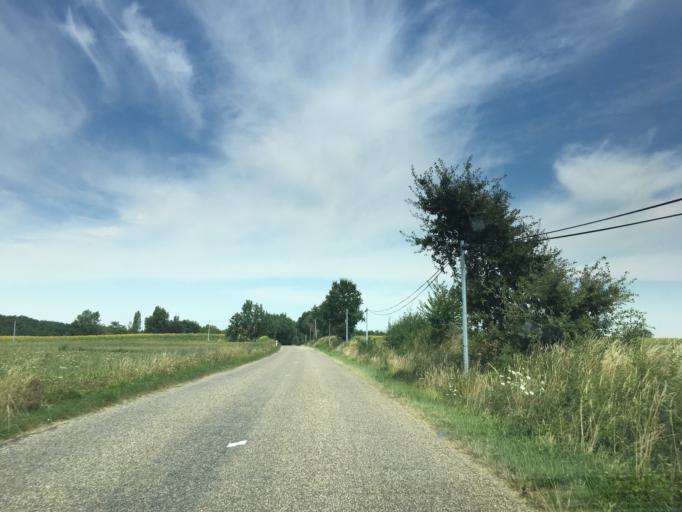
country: FR
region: Midi-Pyrenees
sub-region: Departement du Gers
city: Fleurance
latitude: 43.8185
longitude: 0.6342
